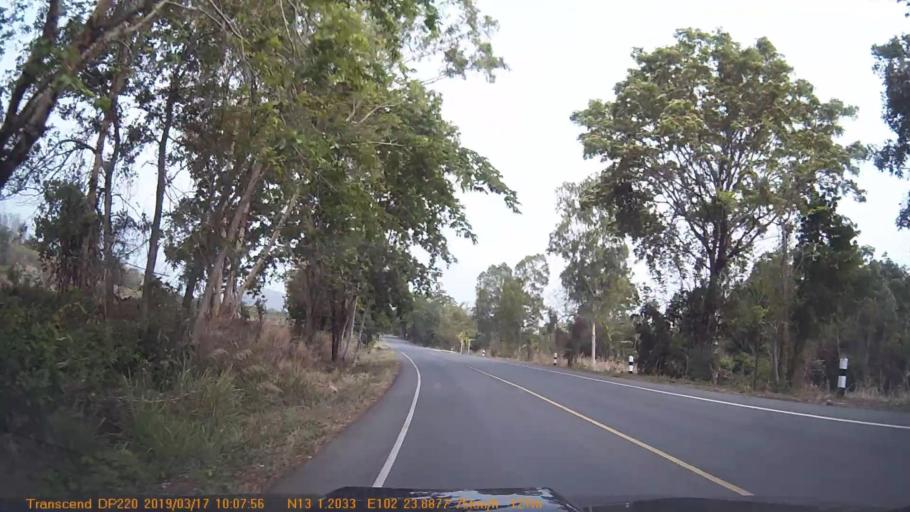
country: TH
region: Chanthaburi
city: Pong Nam Ron
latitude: 13.0223
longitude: 102.3973
